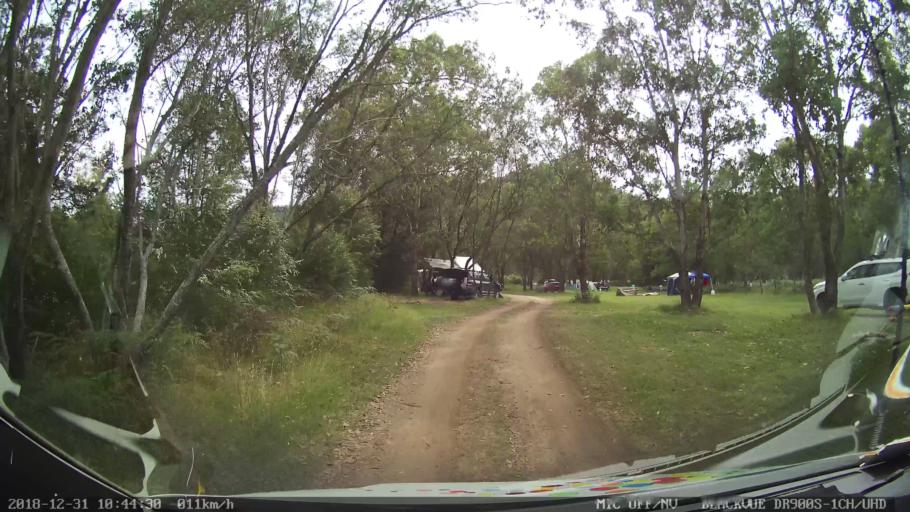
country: AU
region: New South Wales
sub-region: Snowy River
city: Jindabyne
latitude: -36.3788
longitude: 148.1783
